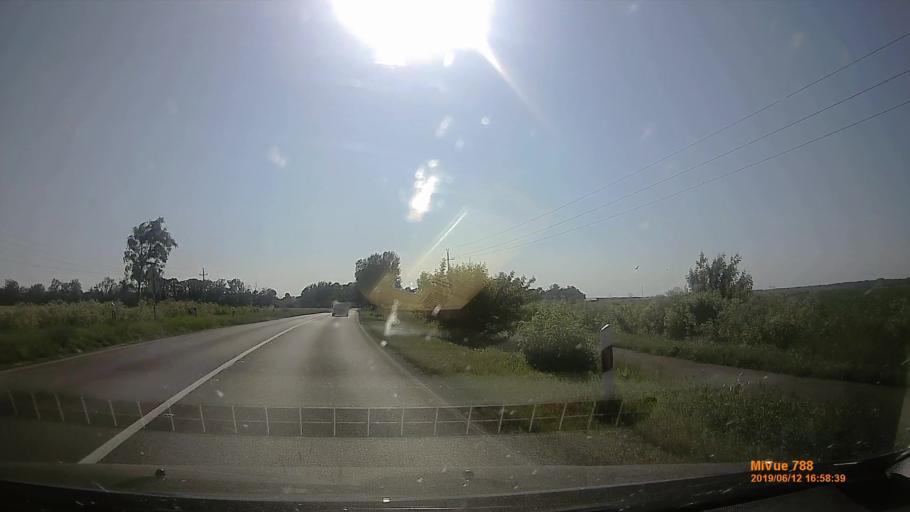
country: HU
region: Csongrad
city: Deszk
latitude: 46.2172
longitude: 20.2798
